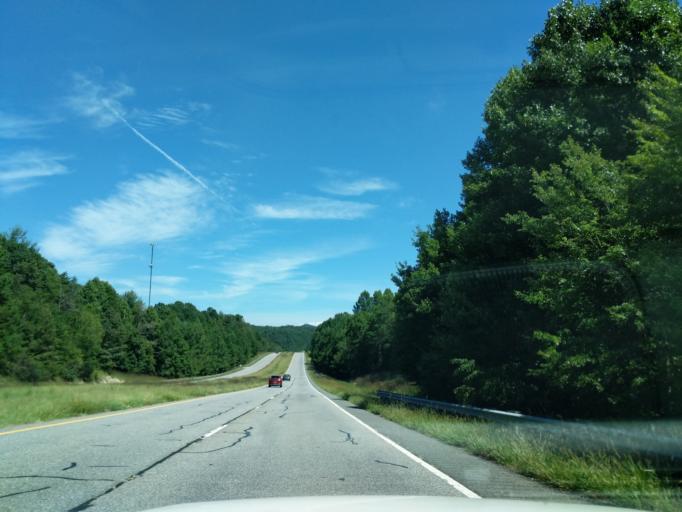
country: US
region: Georgia
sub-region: Fannin County
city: Blue Ridge
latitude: 34.8894
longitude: -84.2000
